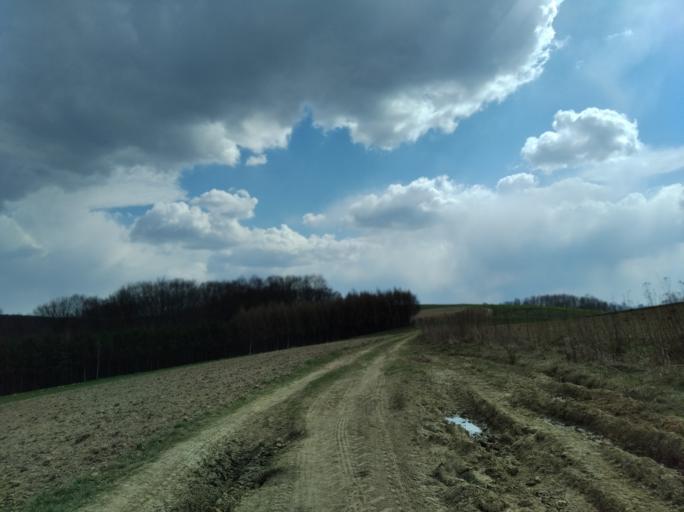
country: PL
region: Subcarpathian Voivodeship
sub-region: Powiat strzyzowski
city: Strzyzow
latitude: 49.9154
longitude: 21.7464
